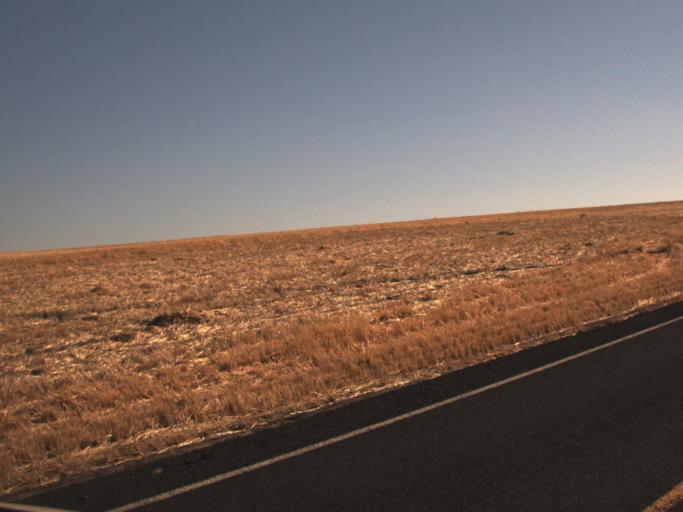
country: US
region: Washington
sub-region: Adams County
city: Ritzville
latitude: 46.9259
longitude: -118.5671
